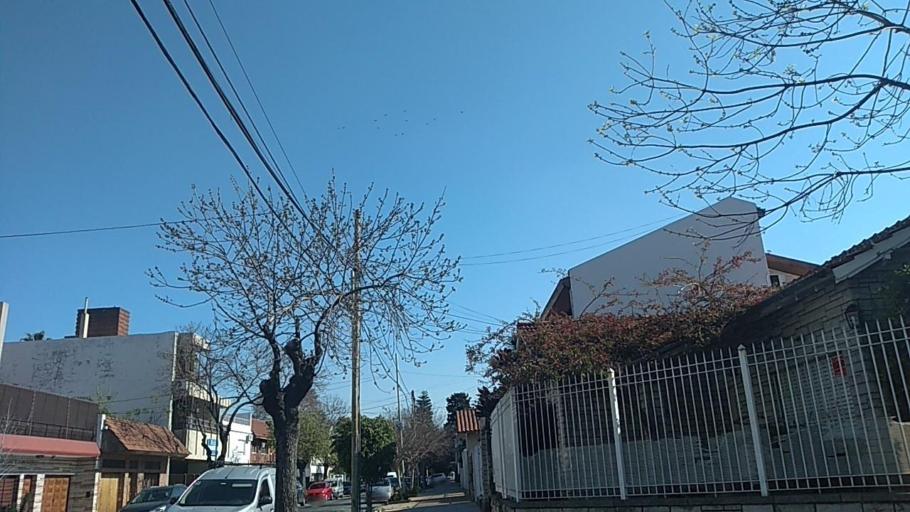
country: AR
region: Buenos Aires F.D.
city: Villa Santa Rita
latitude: -34.6052
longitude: -58.5018
